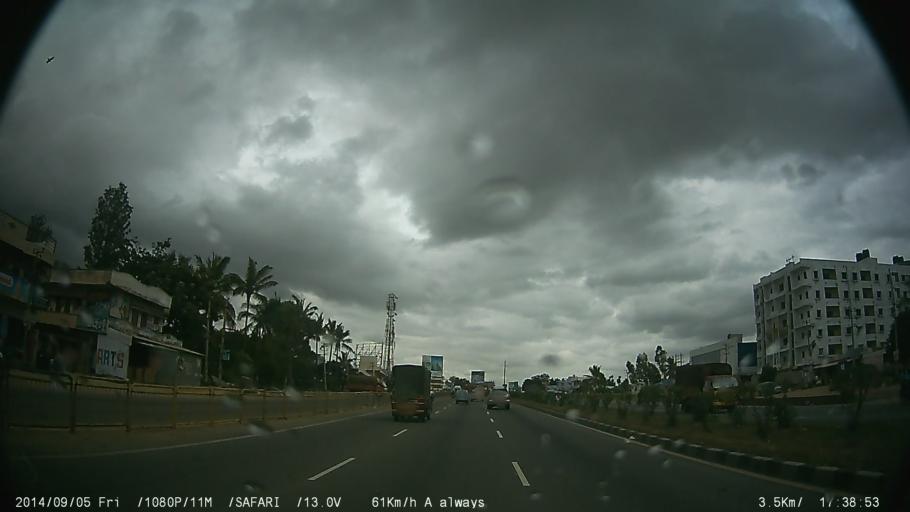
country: IN
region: Karnataka
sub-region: Bangalore Urban
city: Anekal
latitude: 12.7926
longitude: 77.7269
